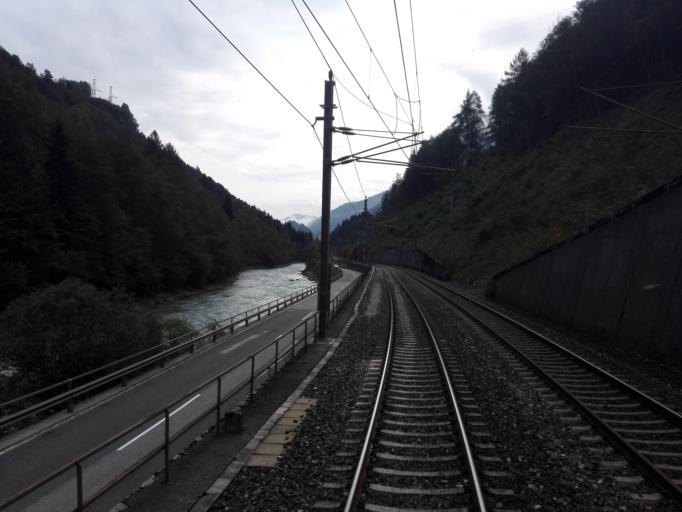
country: AT
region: Salzburg
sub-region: Politischer Bezirk Zell am See
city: Lend
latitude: 47.2985
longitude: 13.0774
